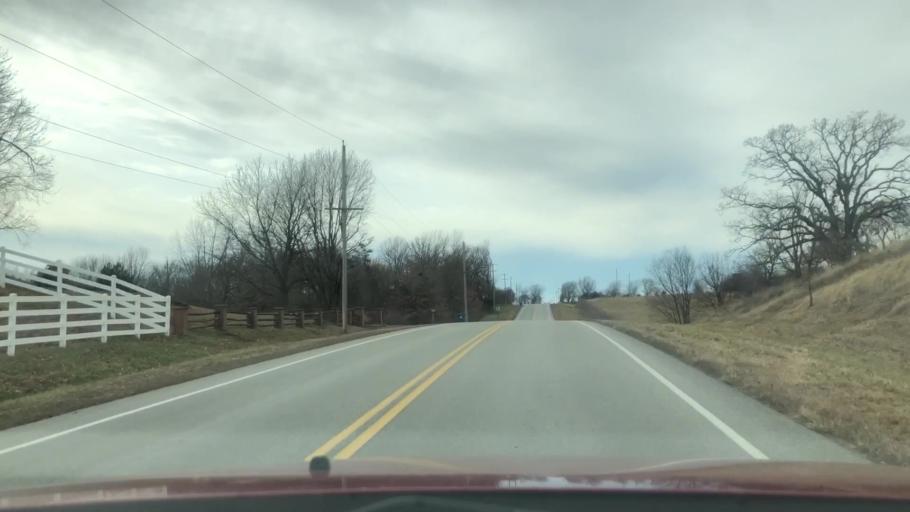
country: US
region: Missouri
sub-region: Greene County
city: Springfield
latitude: 37.2728
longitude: -93.2333
